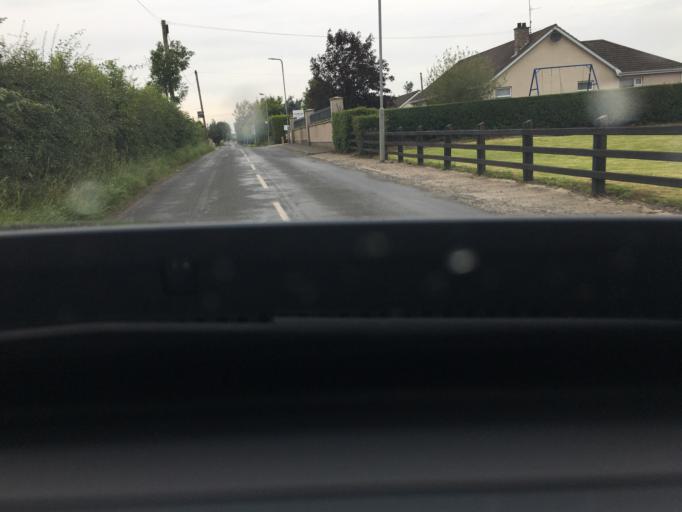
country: GB
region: Northern Ireland
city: Coalisland
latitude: 54.5374
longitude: -6.6194
